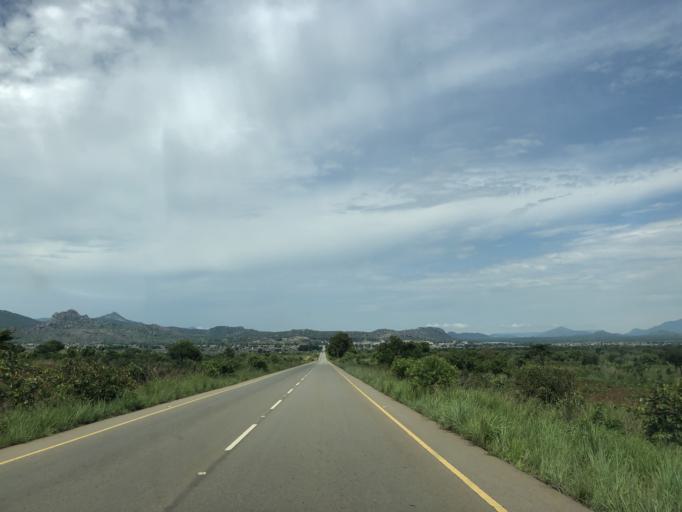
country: AO
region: Cuanza Sul
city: Quibala
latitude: -10.7338
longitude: 15.0124
